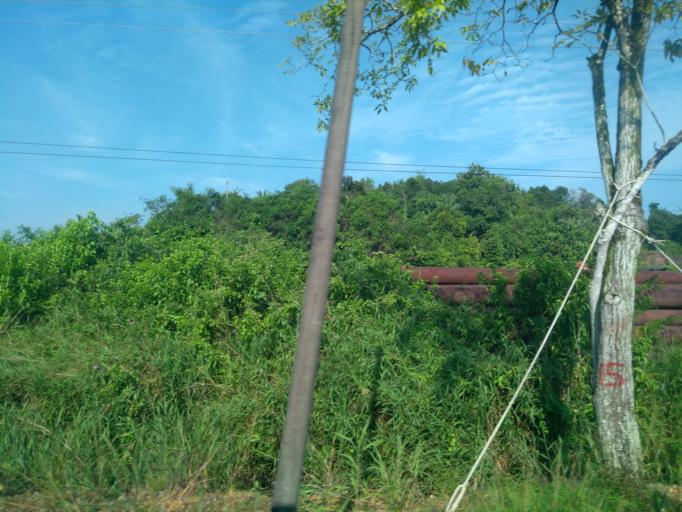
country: MY
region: Sarawak
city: Kuching
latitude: 1.6512
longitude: 110.4455
